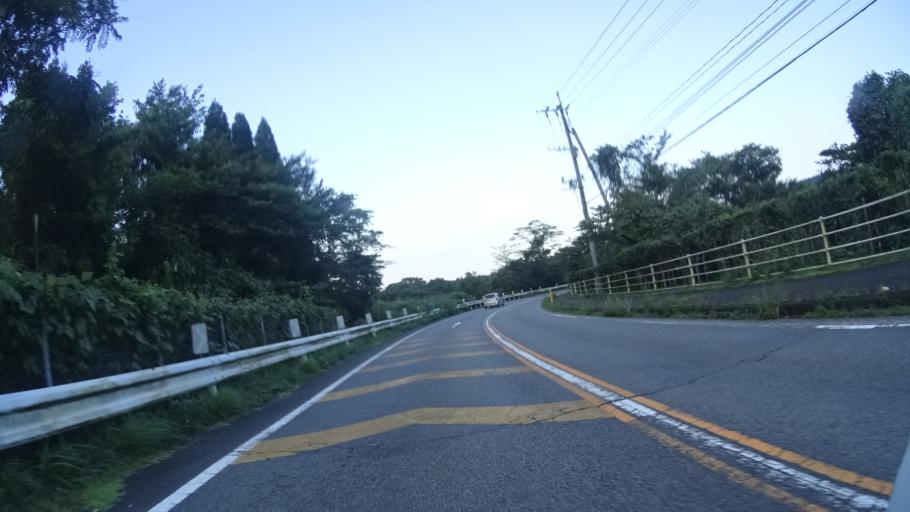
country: JP
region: Oita
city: Beppu
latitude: 33.3498
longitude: 131.4372
